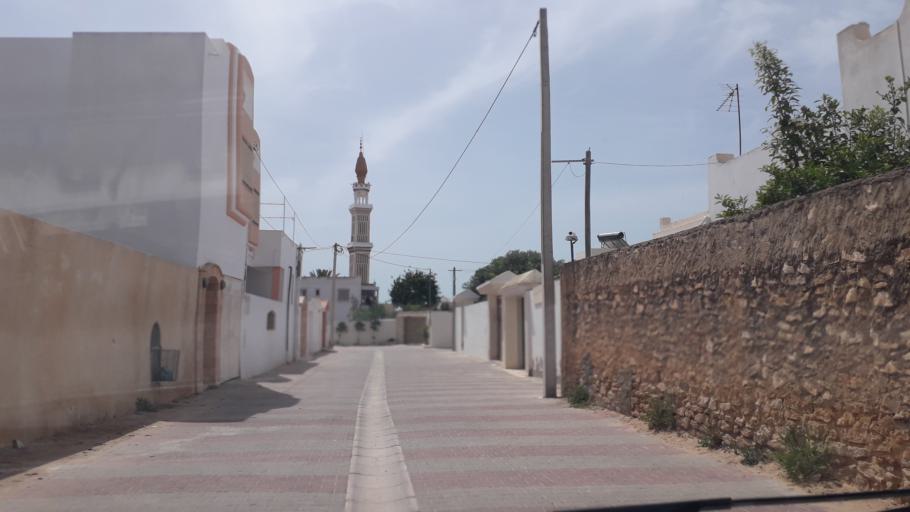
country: TN
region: Safaqis
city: Al Qarmadah
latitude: 34.8015
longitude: 10.7663
